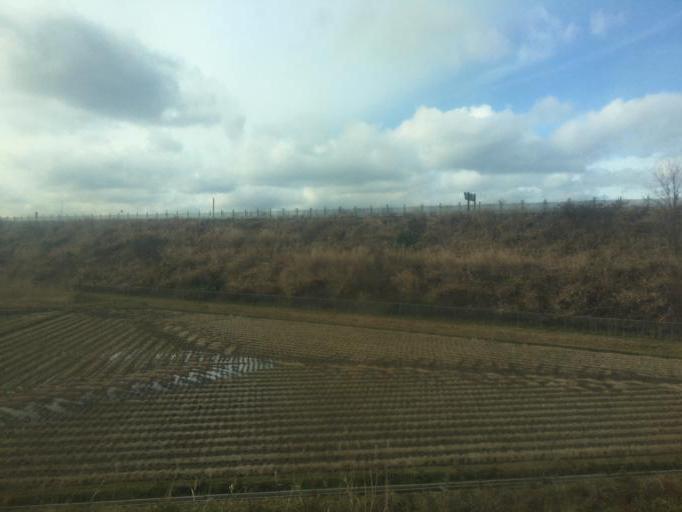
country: JP
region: Akita
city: Noshiromachi
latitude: 40.1763
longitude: 140.0585
